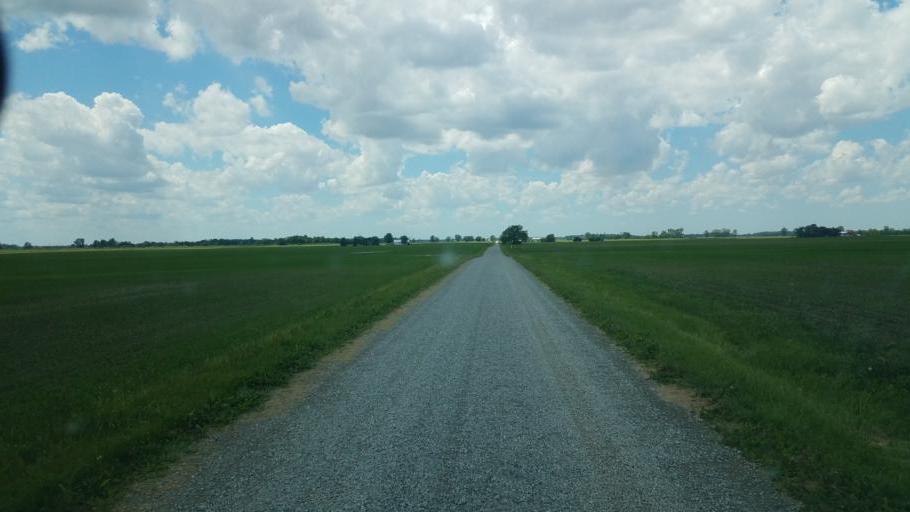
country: US
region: Ohio
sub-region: Wyandot County
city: Upper Sandusky
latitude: 40.7600
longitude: -83.2477
